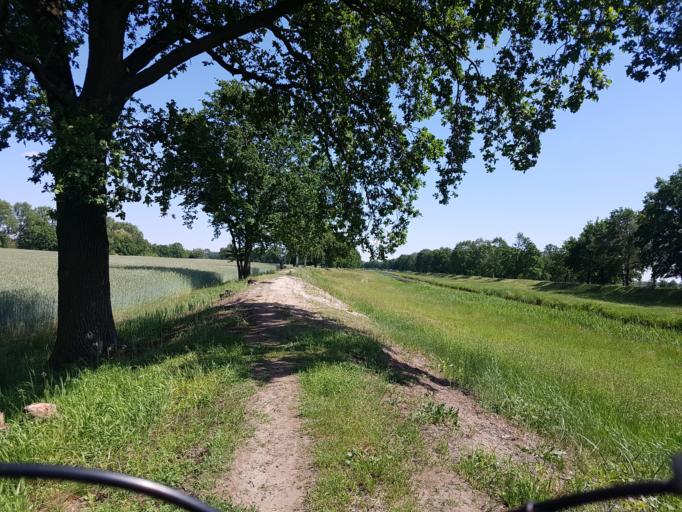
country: DE
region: Brandenburg
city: Elsterwerda
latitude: 51.4599
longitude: 13.4899
